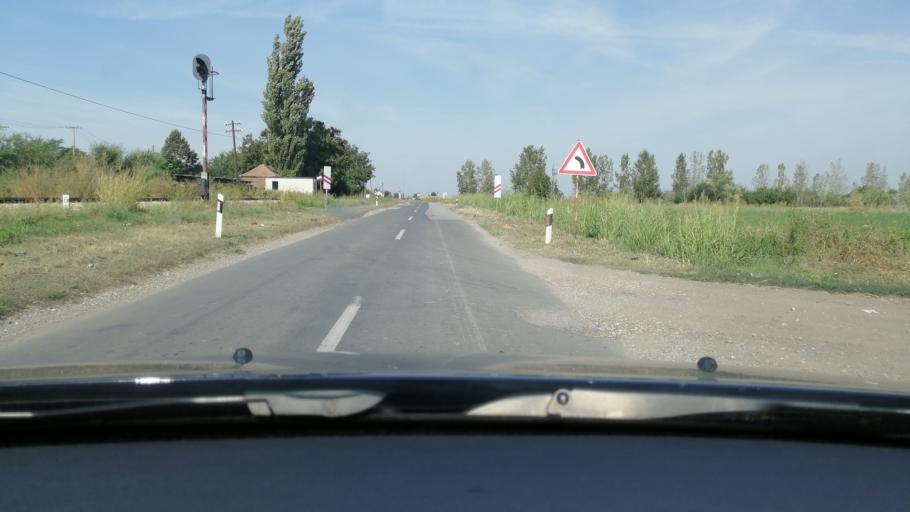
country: RS
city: Orlovat
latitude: 45.2497
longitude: 20.5885
